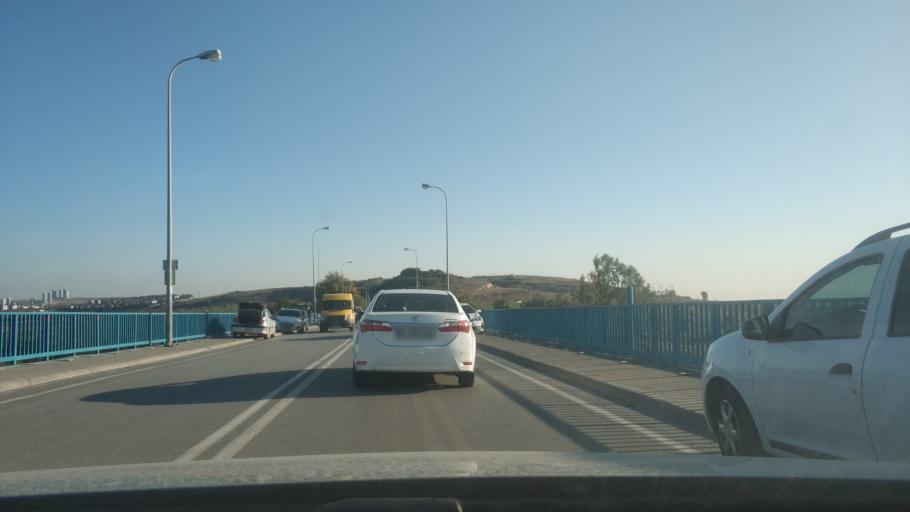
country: TR
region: Adana
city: Adana
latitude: 37.0992
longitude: 35.3038
